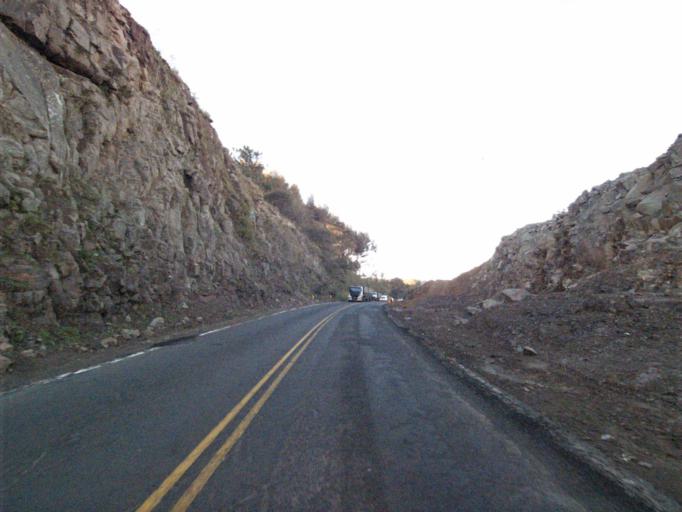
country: AR
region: Misiones
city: Bernardo de Irigoyen
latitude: -26.3579
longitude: -53.5368
